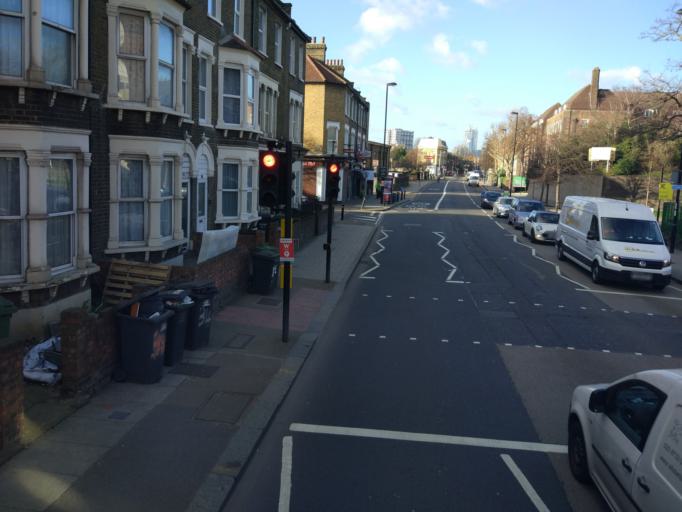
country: GB
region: England
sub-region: Greater London
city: Poplar
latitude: 51.4888
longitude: -0.0400
